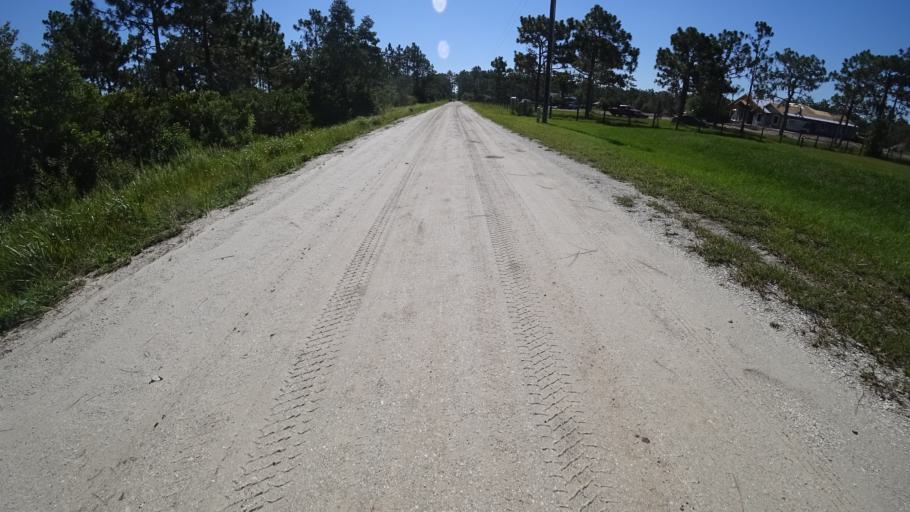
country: US
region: Florida
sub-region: Sarasota County
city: Fruitville
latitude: 27.3978
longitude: -82.2910
